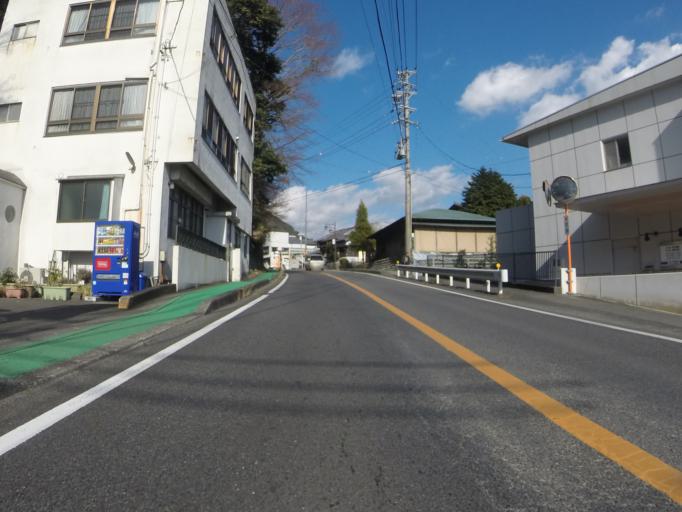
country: JP
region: Shizuoka
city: Fujinomiya
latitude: 35.0964
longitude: 138.5131
